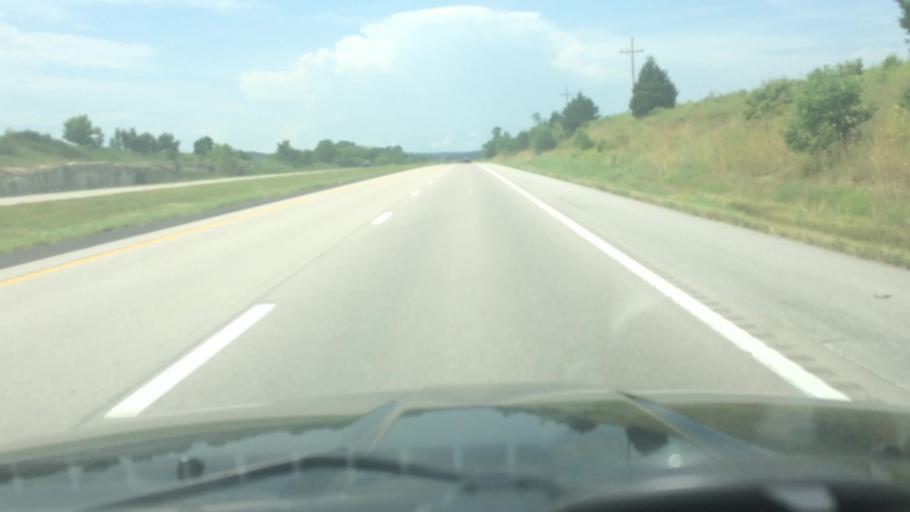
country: US
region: Missouri
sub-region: Polk County
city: Humansville
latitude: 37.8018
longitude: -93.5959
